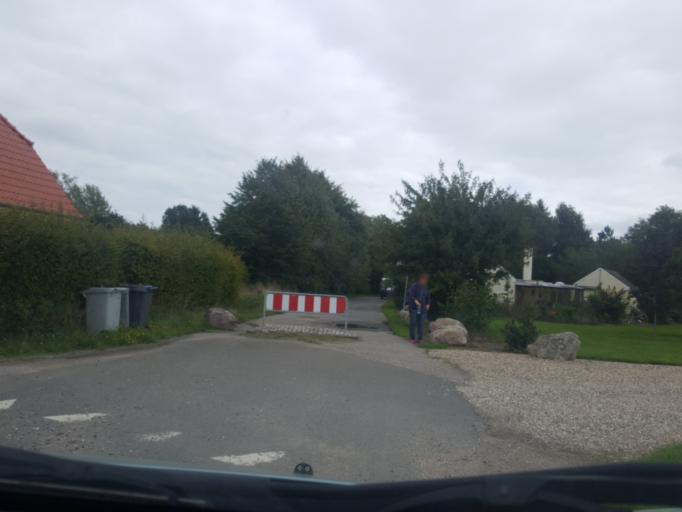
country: DK
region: Zealand
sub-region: Soro Kommune
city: Soro
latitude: 55.4463
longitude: 11.5311
